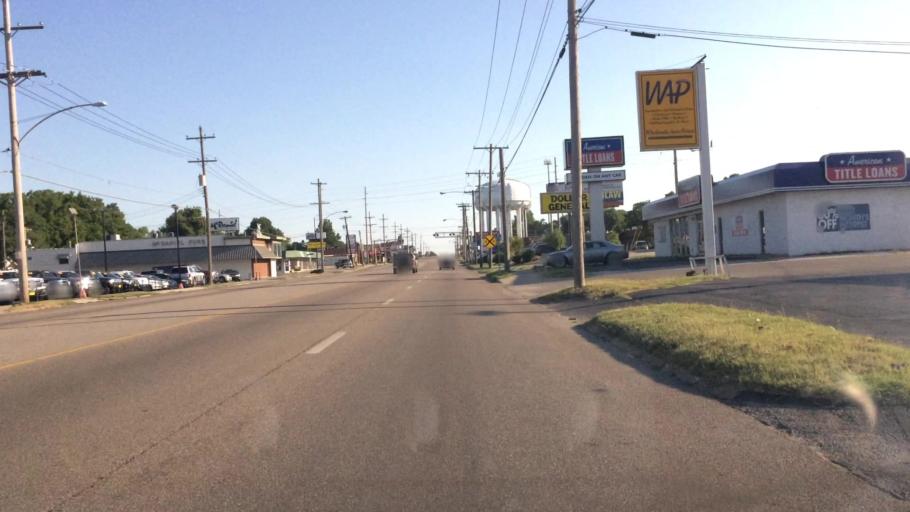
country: US
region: Missouri
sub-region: Greene County
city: Springfield
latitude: 37.1970
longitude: -93.2620
